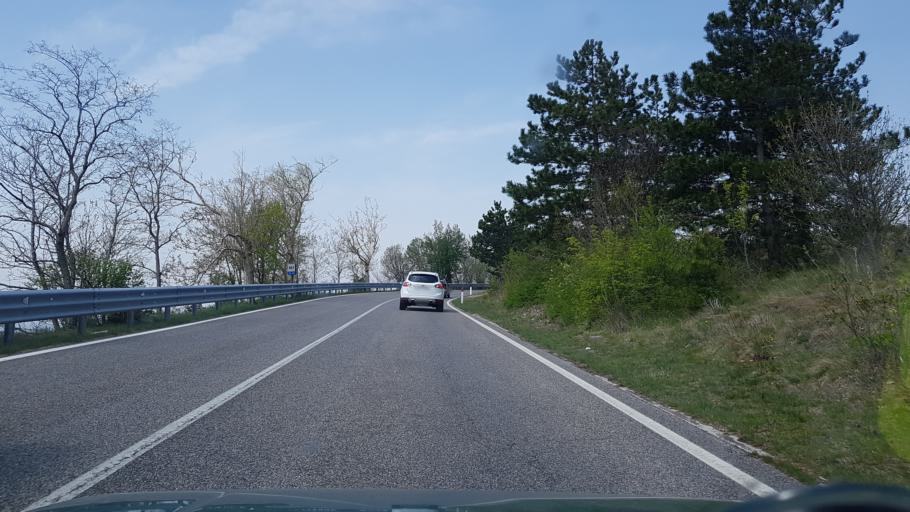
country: SI
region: Hrpelje-Kozina
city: Kozina
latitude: 45.6283
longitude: 13.8948
